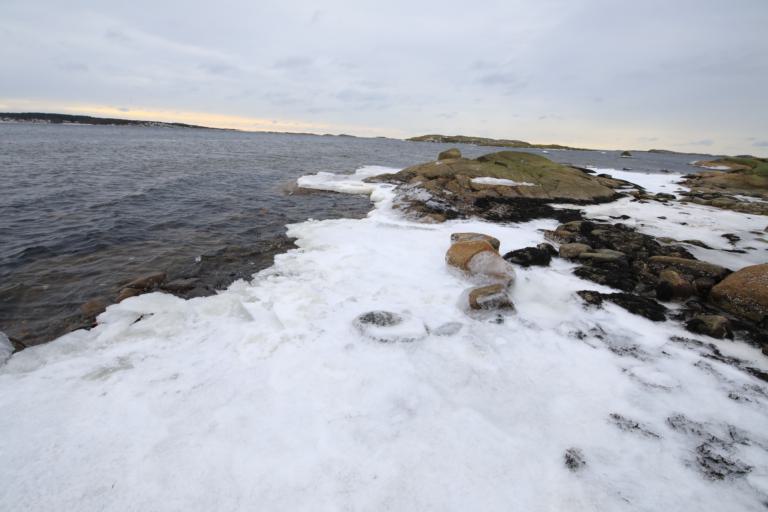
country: SE
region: Halland
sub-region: Kungsbacka Kommun
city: Frillesas
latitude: 57.2137
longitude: 12.1706
